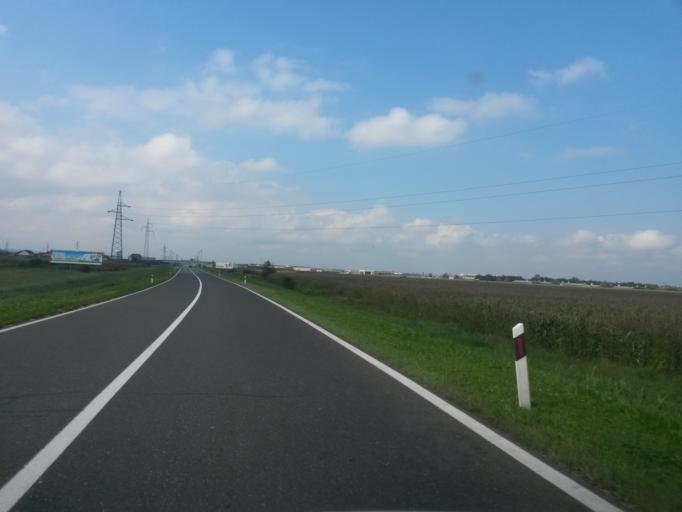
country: HR
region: Varazdinska
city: Varazdin
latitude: 46.2639
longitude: 16.3905
